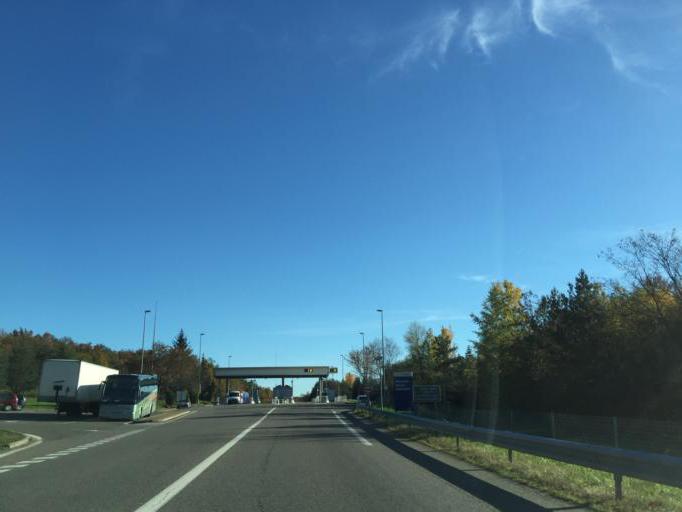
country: FR
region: Rhone-Alpes
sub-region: Departement de la Loire
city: Saint-Germain-Laval
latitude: 45.8619
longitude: 4.0408
